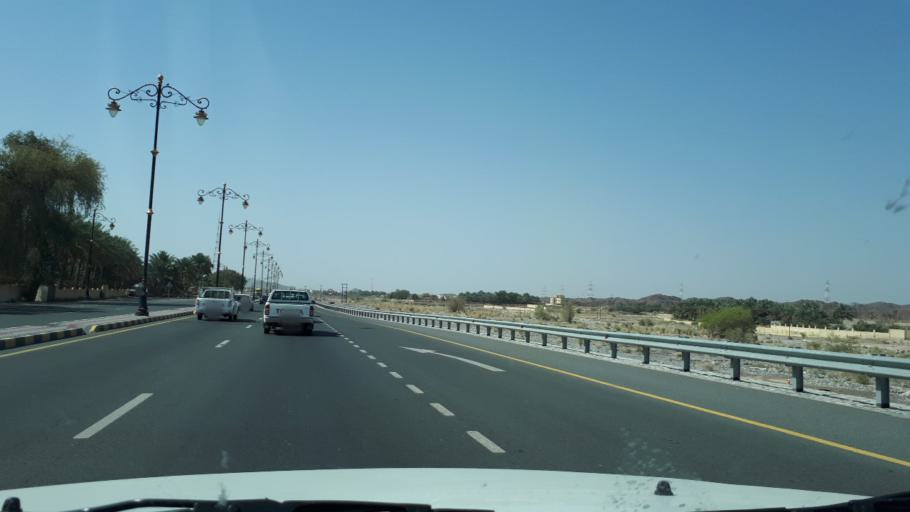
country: OM
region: Muhafazat ad Dakhiliyah
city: Nizwa
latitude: 22.8868
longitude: 57.5256
